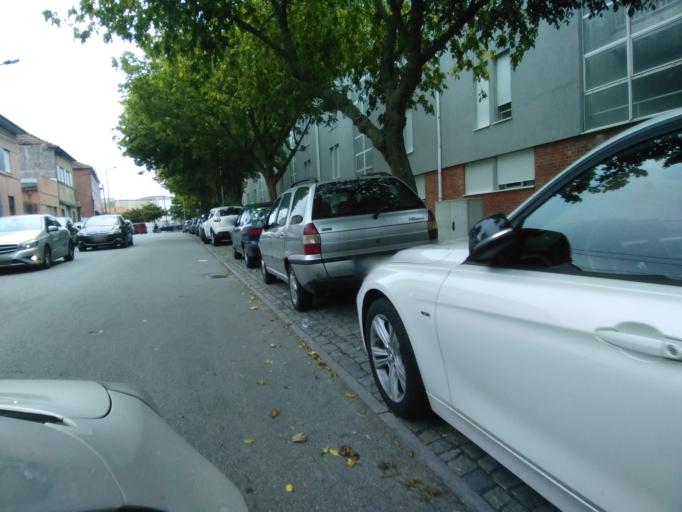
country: PT
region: Porto
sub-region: Matosinhos
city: Santa Cruz do Bispo
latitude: 41.2245
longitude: -8.7002
